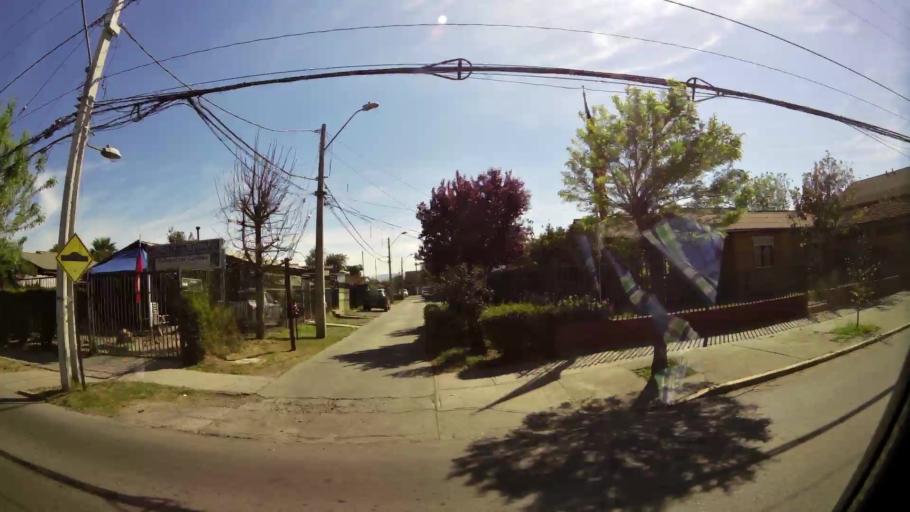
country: CL
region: Santiago Metropolitan
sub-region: Provincia de Santiago
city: Lo Prado
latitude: -33.5029
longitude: -70.7176
